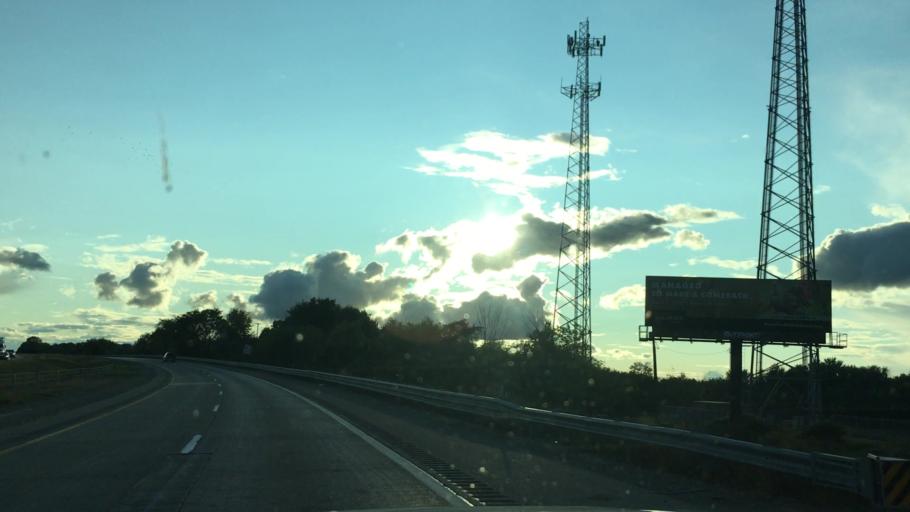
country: US
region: Michigan
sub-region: Kent County
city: Lowell
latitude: 42.8790
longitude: -85.3077
